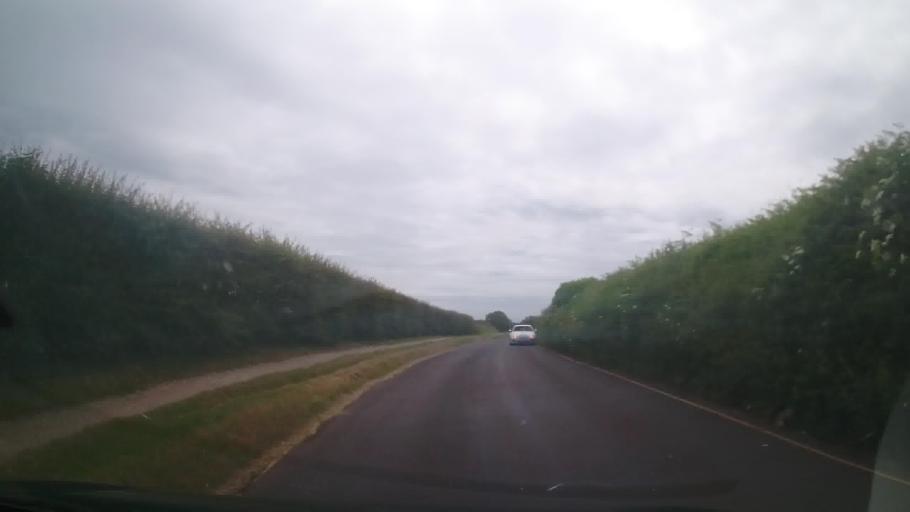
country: GB
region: England
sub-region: Devon
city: Dartmouth
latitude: 50.2889
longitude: -3.6517
